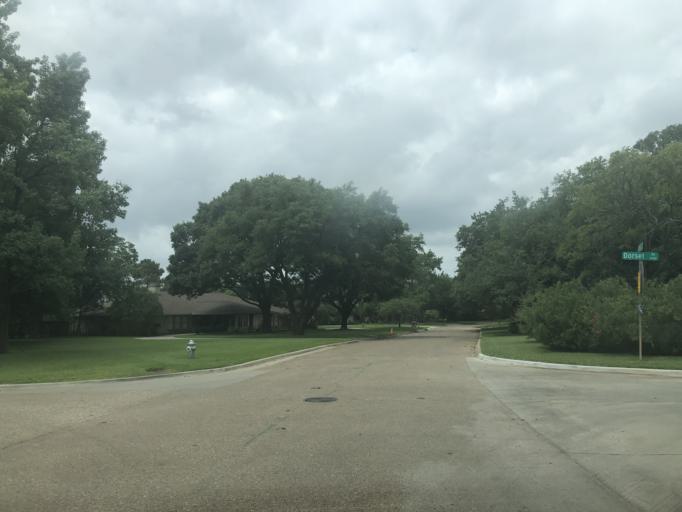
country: US
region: Texas
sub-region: Dallas County
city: University Park
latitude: 32.8849
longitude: -96.8297
